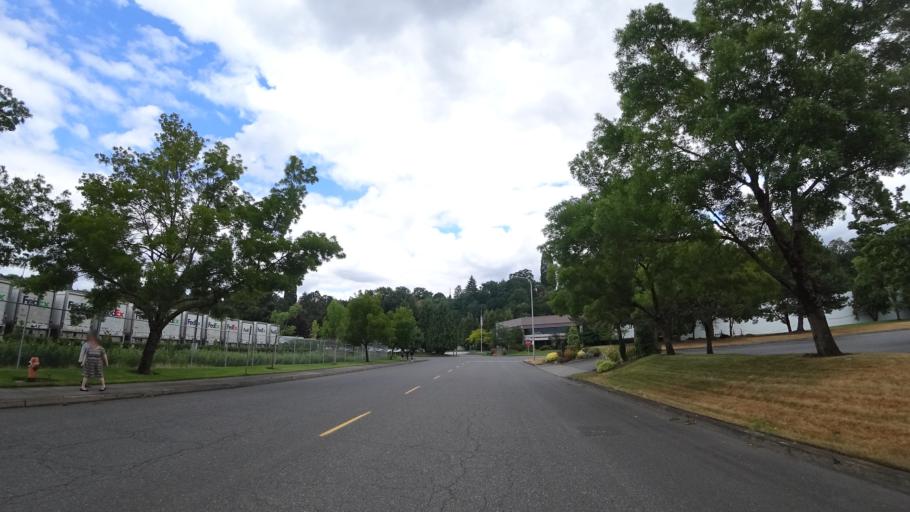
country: US
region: Oregon
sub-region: Multnomah County
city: Portland
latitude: 45.5704
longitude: -122.7039
